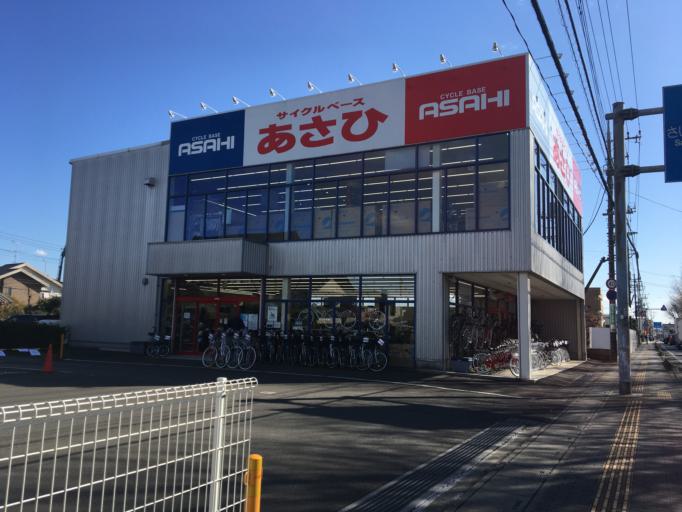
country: JP
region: Saitama
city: Kamifukuoka
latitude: 35.8680
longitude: 139.5066
